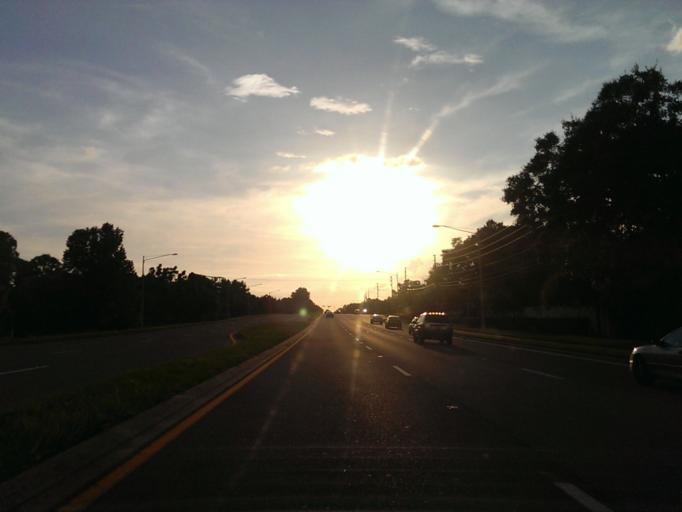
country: US
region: Florida
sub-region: Orange County
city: Bay Hill
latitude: 28.4937
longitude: -81.4788
